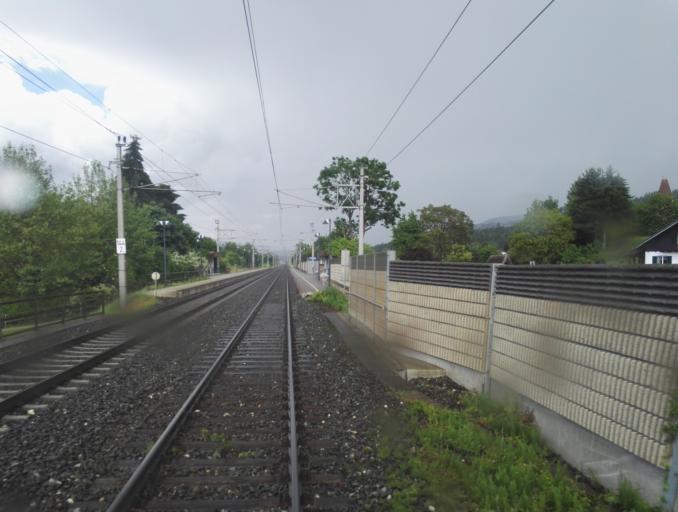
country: AT
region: Styria
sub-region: Politischer Bezirk Bruck-Muerzzuschlag
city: Allerheiligen im Muerztal
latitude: 47.4816
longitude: 15.4023
